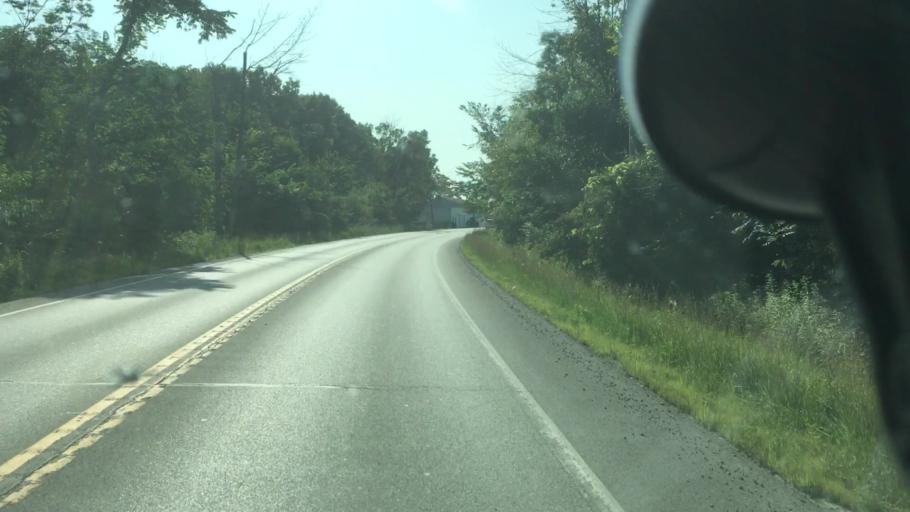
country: US
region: Ohio
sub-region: Mahoning County
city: Lowellville
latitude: 41.0212
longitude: -80.5037
